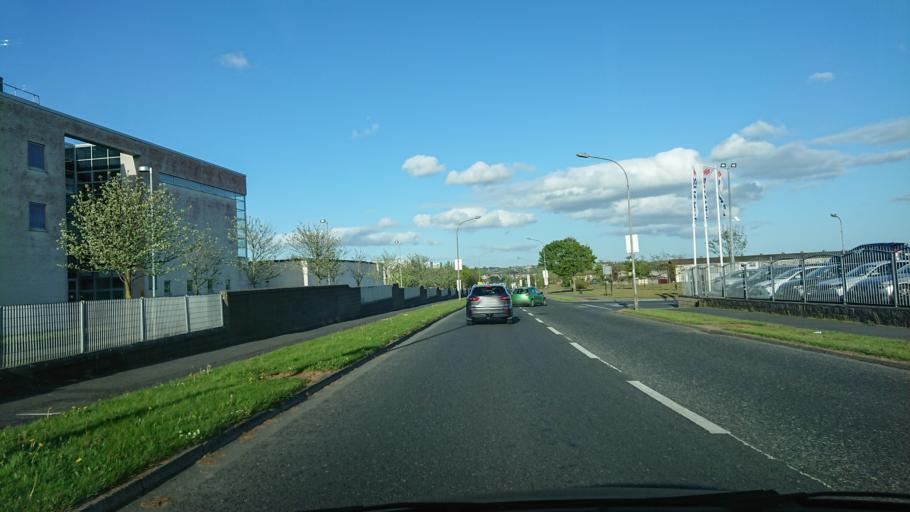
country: IE
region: Munster
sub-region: Waterford
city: Waterford
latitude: 52.2448
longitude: -7.1419
